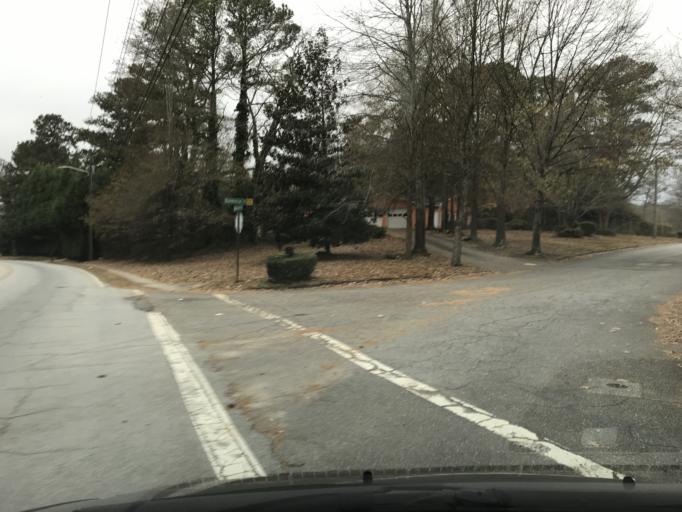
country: US
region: Georgia
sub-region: DeKalb County
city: Doraville
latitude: 33.8767
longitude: -84.2523
